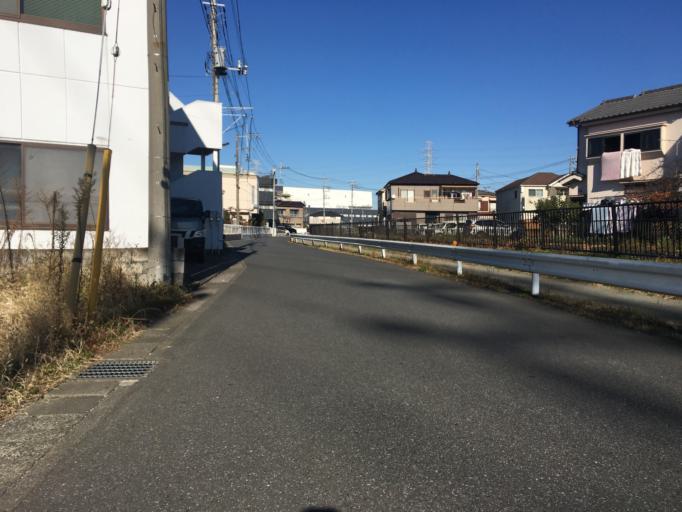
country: JP
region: Saitama
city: Yashio-shi
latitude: 35.8346
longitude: 139.8316
